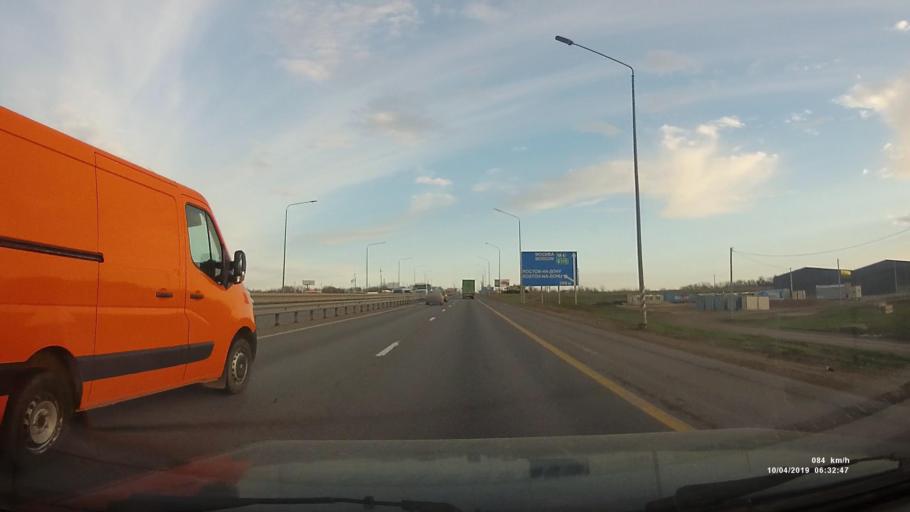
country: RU
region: Rostov
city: Aksay
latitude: 47.2797
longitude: 39.8511
